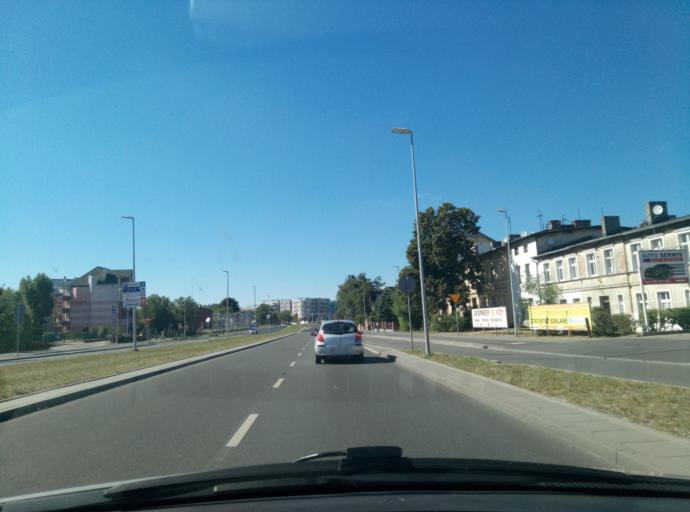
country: PL
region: Kujawsko-Pomorskie
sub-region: Torun
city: Torun
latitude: 53.0229
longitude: 18.5944
